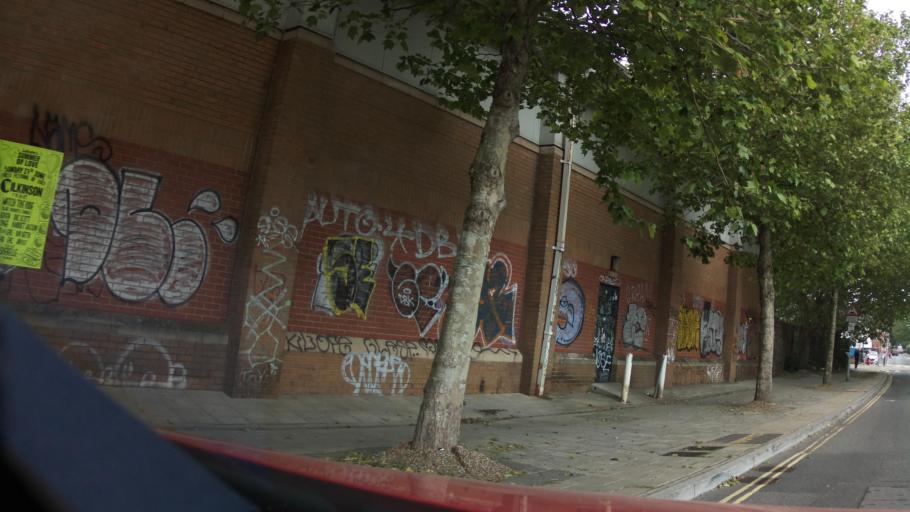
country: GB
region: England
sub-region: Bristol
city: Bristol
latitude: 51.4602
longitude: -2.5821
